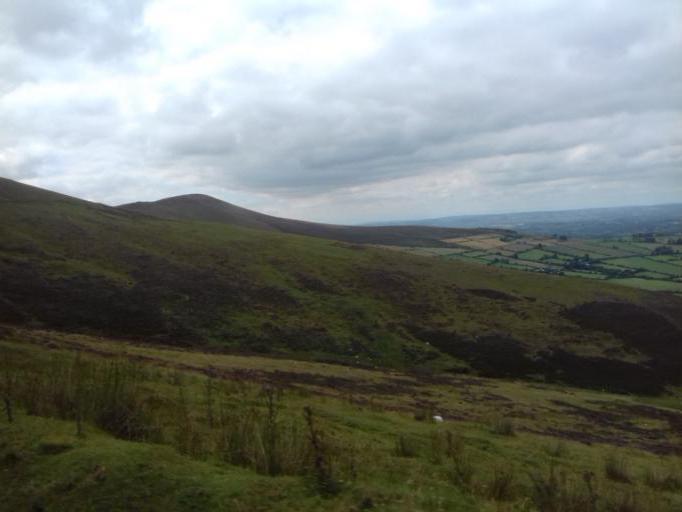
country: IE
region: Leinster
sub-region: Loch Garman
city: Bunclody
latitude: 52.6400
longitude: -6.7758
